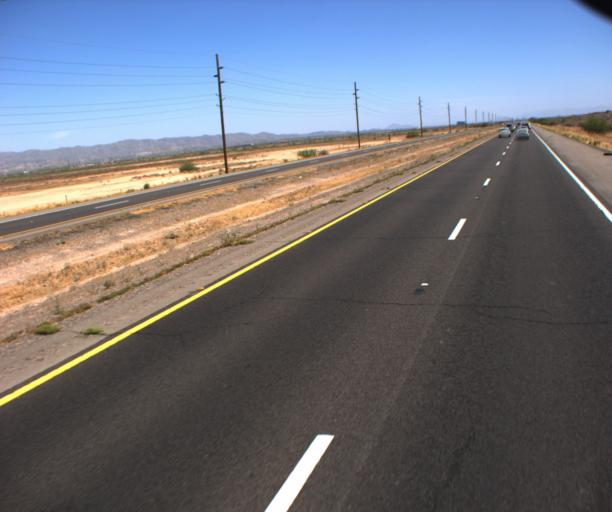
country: US
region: Arizona
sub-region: Maricopa County
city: Sun Lakes
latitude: 33.2281
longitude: -111.9858
